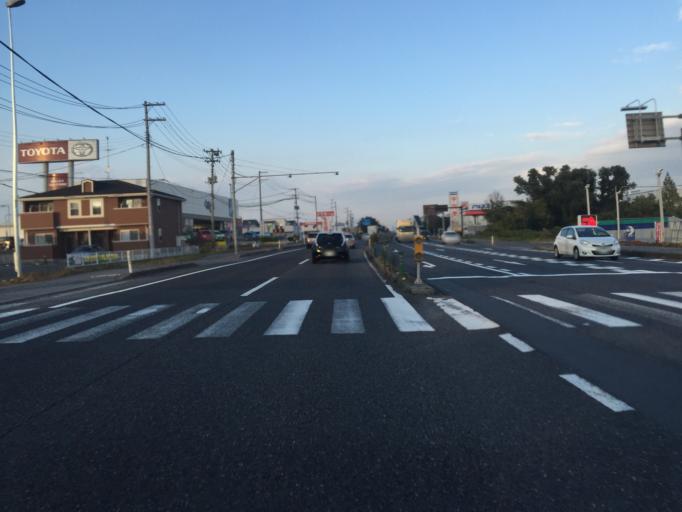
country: JP
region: Fukushima
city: Motomiya
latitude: 37.4891
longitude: 140.3813
